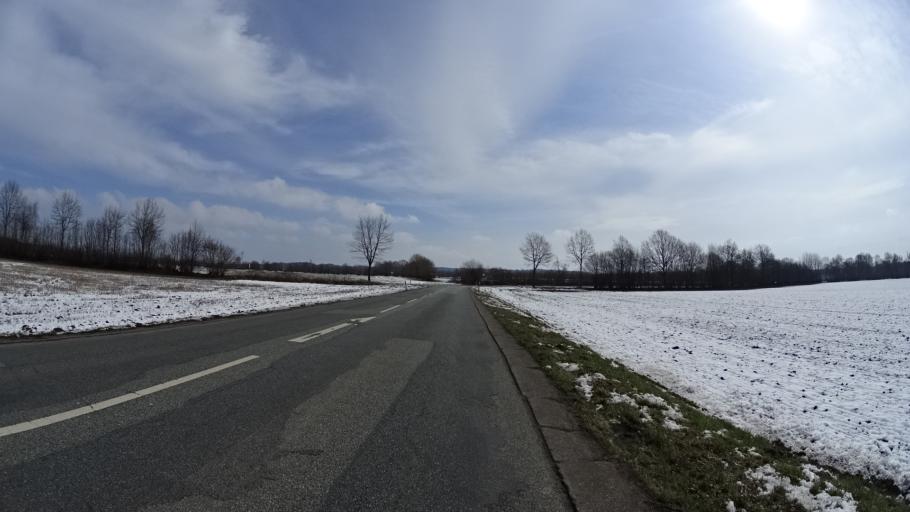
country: DE
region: Schleswig-Holstein
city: Latendorf
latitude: 54.0098
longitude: 10.0586
